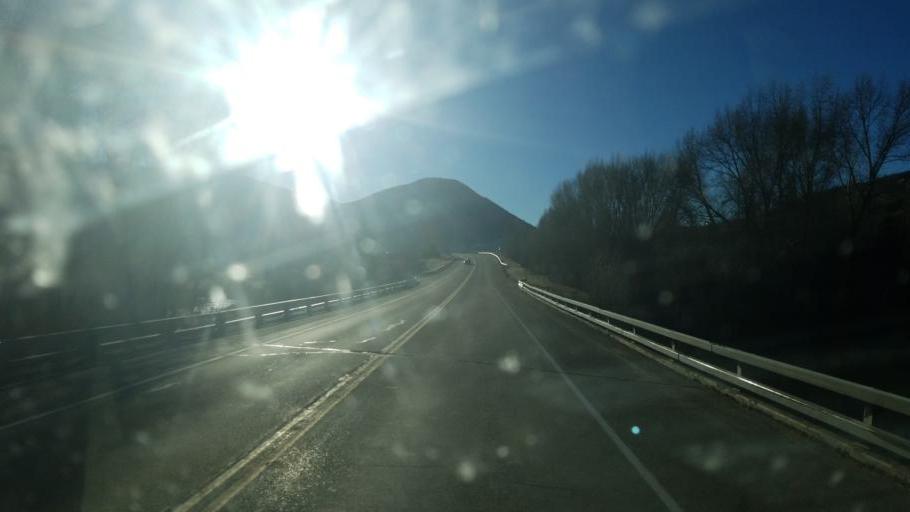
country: US
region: Colorado
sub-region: Gunnison County
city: Crested Butte
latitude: 38.8149
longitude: -106.9051
